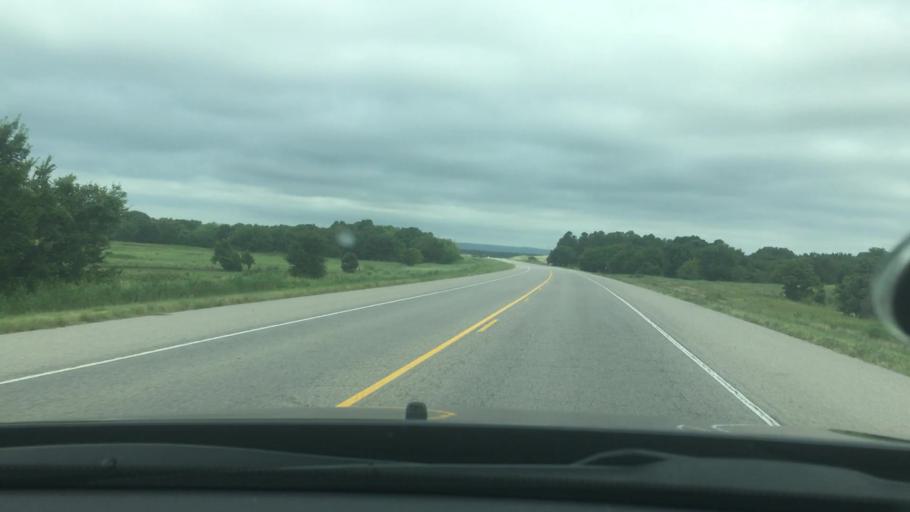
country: US
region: Oklahoma
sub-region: Pontotoc County
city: Ada
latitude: 34.6770
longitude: -96.5765
